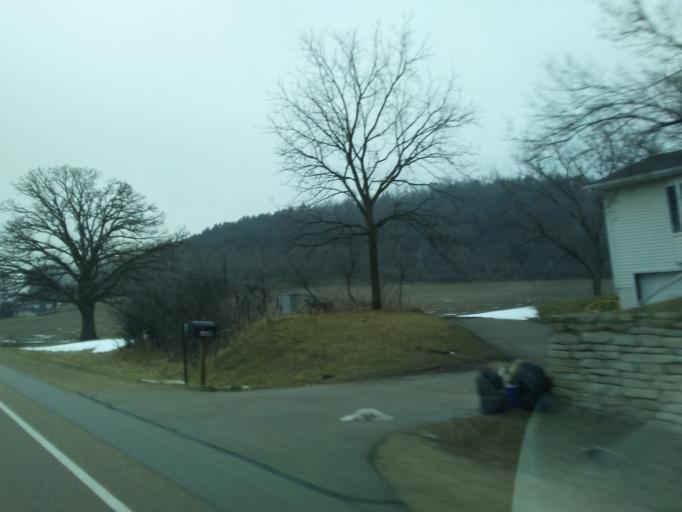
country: US
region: Wisconsin
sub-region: Dane County
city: Black Earth
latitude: 43.1464
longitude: -89.7576
